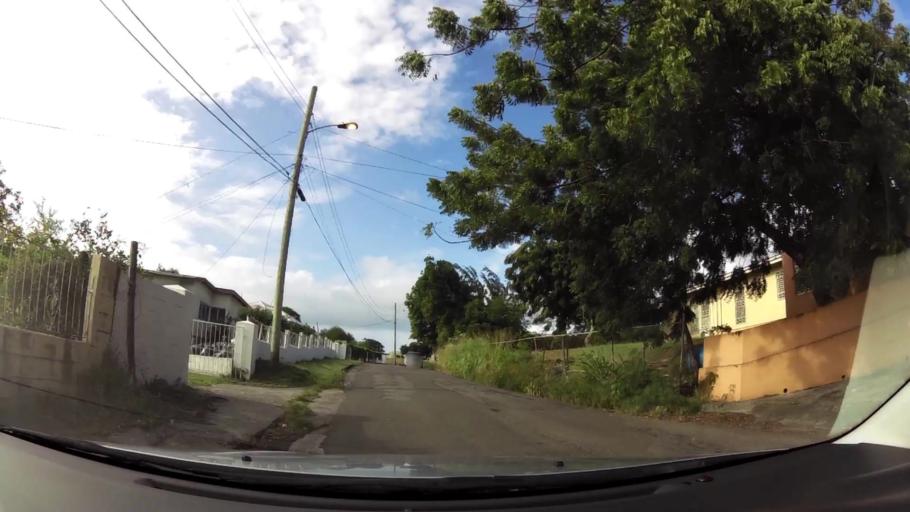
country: AG
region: Saint John
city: Saint John's
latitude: 17.1268
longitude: -61.8352
